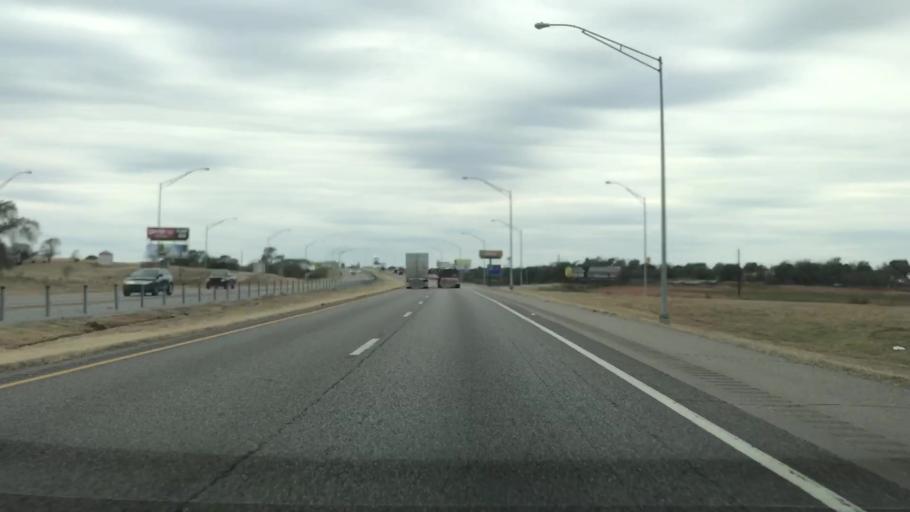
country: US
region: Oklahoma
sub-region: Custer County
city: Clinton
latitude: 35.5006
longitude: -98.9669
